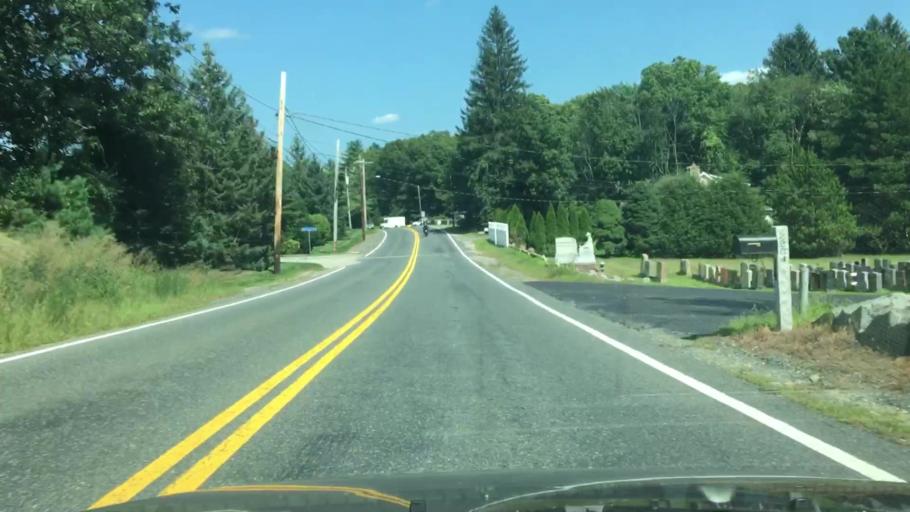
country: US
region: Massachusetts
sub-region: Worcester County
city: Milford
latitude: 42.1692
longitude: -71.4764
